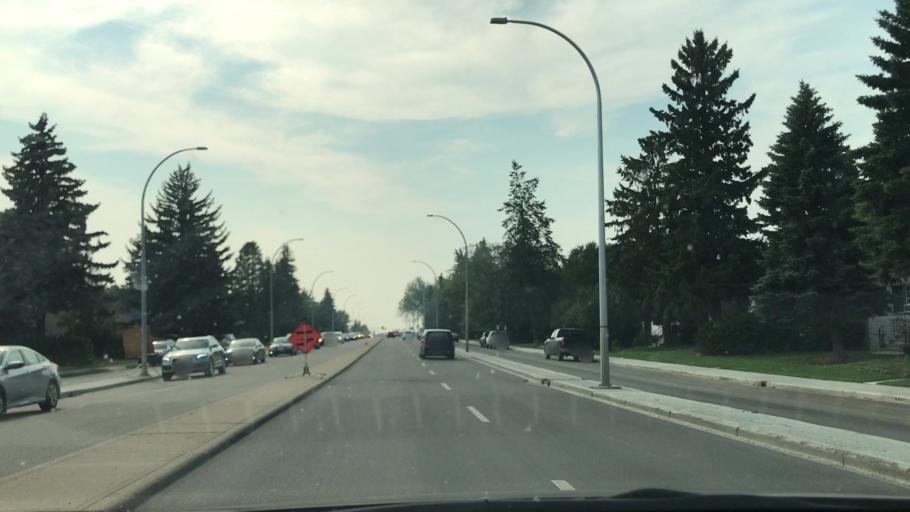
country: CA
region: Alberta
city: Edmonton
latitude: 53.4982
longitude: -113.5055
